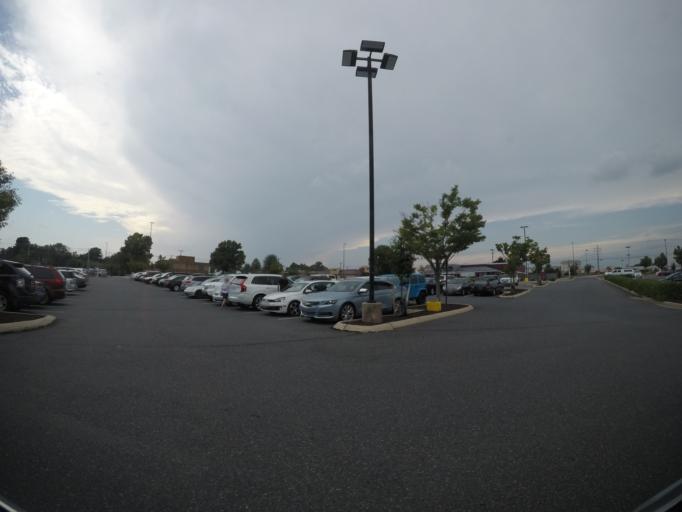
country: US
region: Maryland
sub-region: Harford County
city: Bel Air
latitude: 39.5243
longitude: -76.3542
